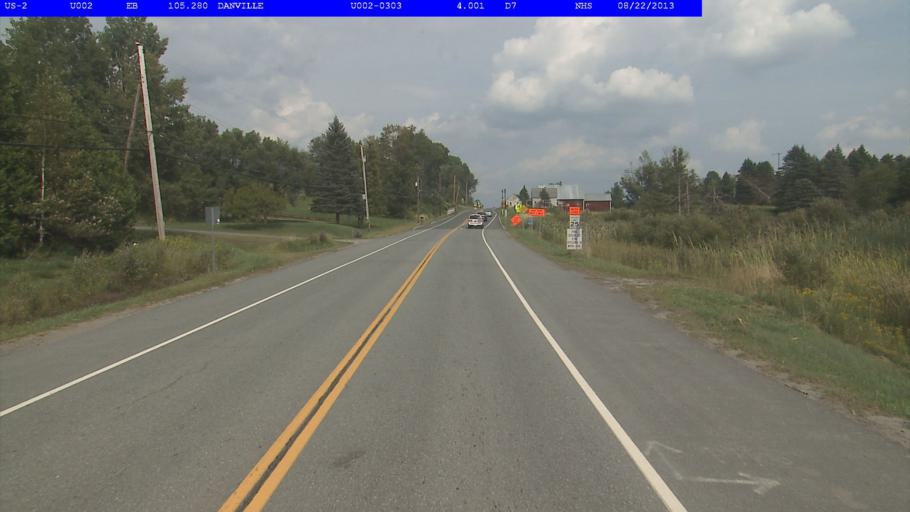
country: US
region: Vermont
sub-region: Caledonia County
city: Saint Johnsbury
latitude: 44.4108
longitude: -72.1493
